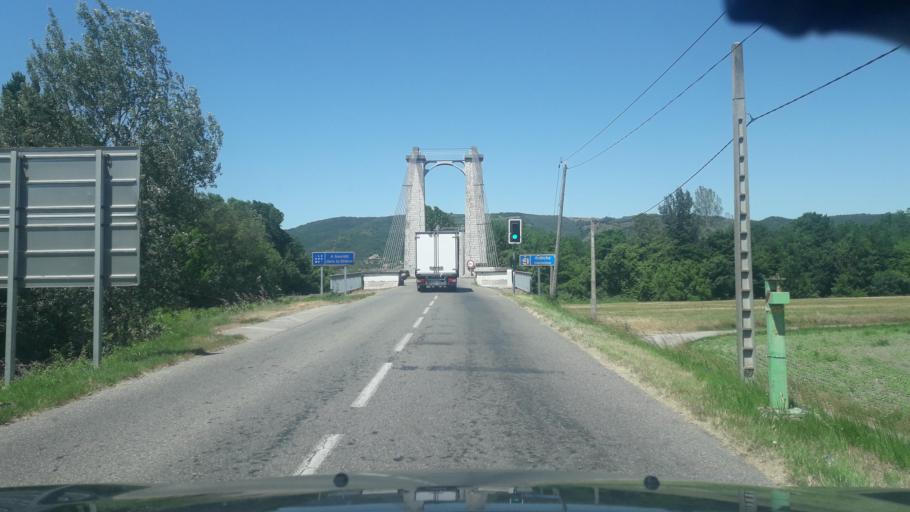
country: FR
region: Rhone-Alpes
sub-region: Departement de l'Ardeche
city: La Voulte-sur-Rhone
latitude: 44.7946
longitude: 4.7979
